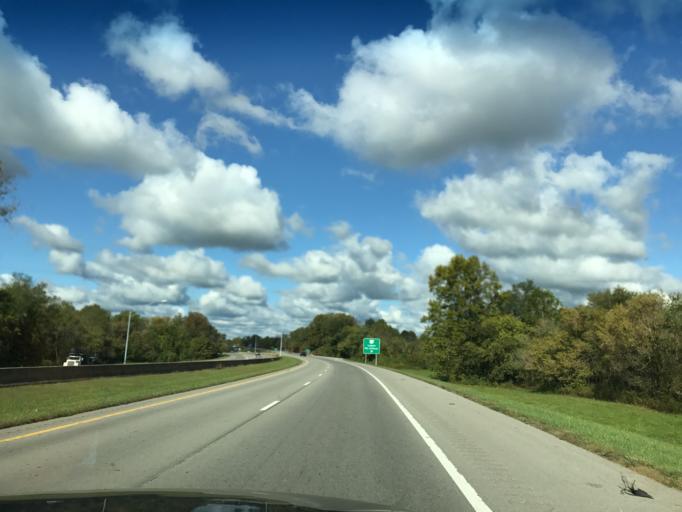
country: US
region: Ohio
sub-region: Hocking County
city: Logan
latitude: 39.5335
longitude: -82.3989
